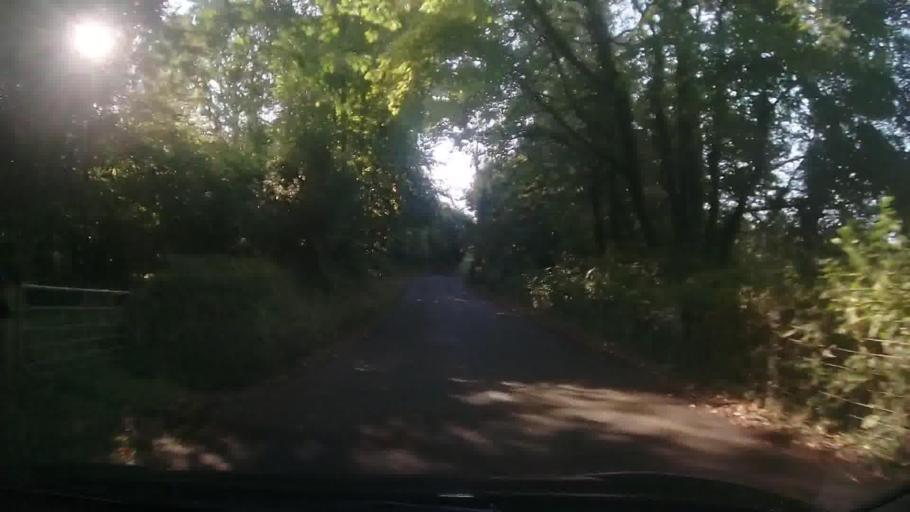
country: GB
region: England
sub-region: Cumbria
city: Seascale
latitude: 54.3952
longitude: -3.3786
